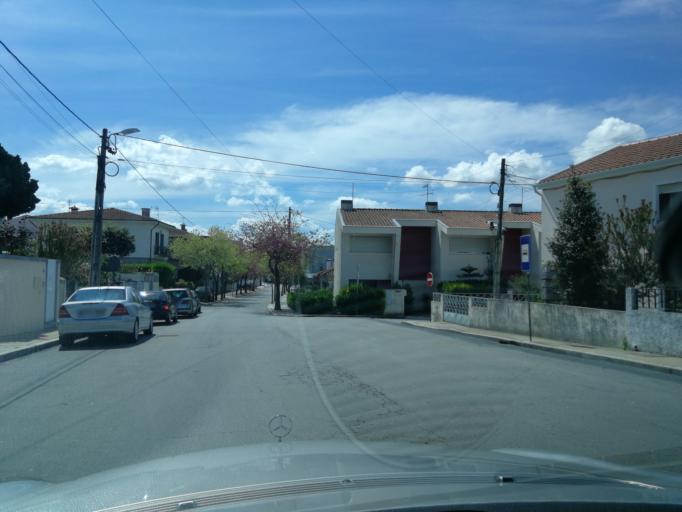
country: PT
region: Braga
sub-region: Vila Nova de Famalicao
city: Vila Nova de Famalicao
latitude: 41.4161
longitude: -8.5159
